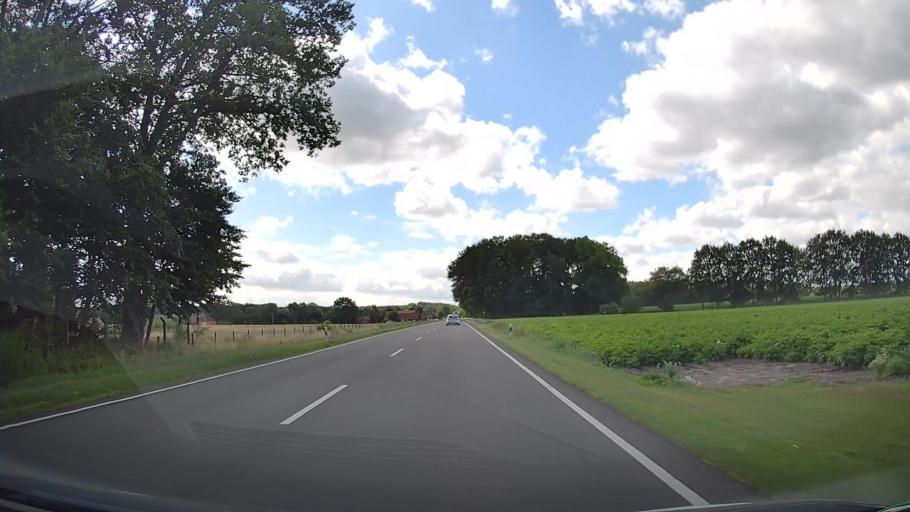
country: DE
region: Lower Saxony
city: Vechta
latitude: 52.6678
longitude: 8.3281
